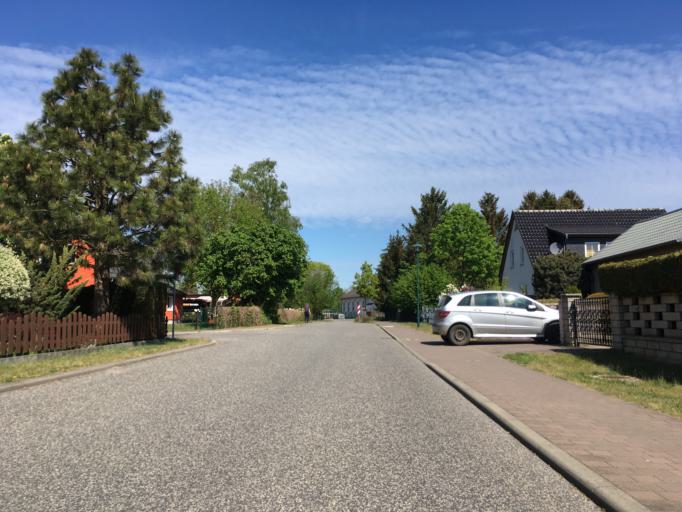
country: DE
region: Berlin
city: Buch
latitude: 52.6729
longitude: 13.5306
